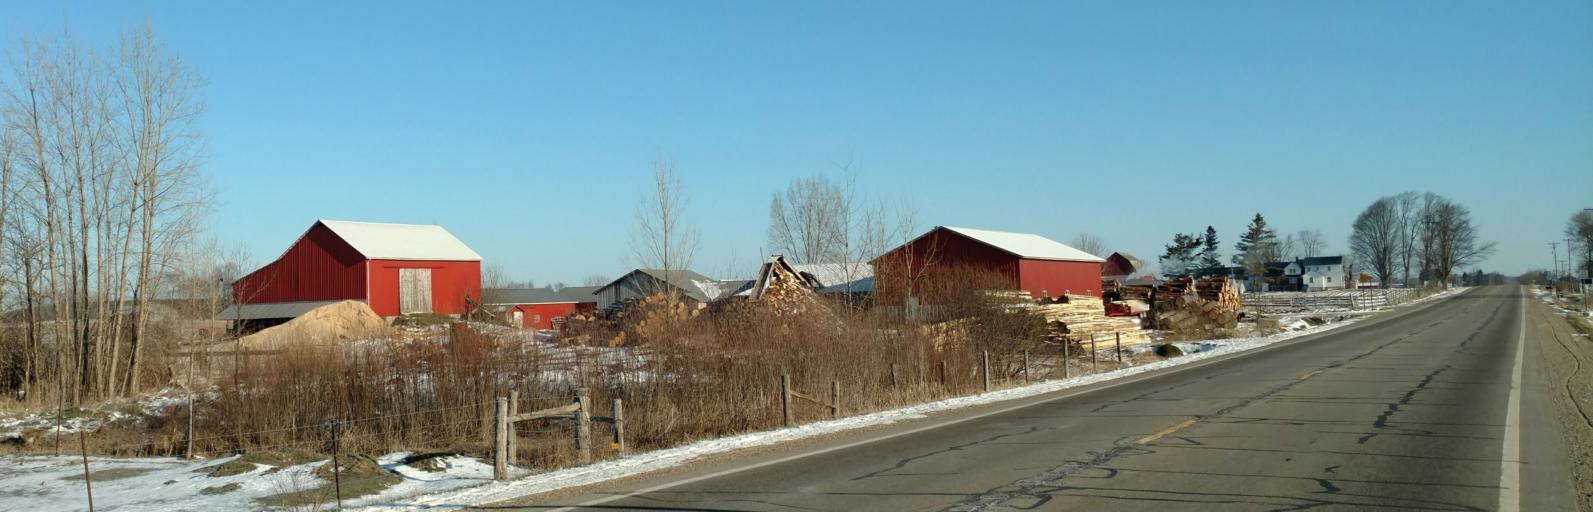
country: US
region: Michigan
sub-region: Gladwin County
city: Gladwin
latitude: 44.0417
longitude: -84.4866
